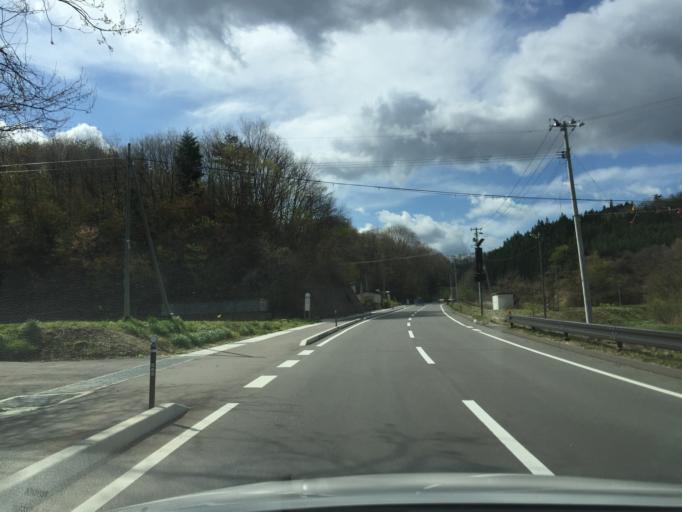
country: JP
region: Fukushima
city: Funehikimachi-funehiki
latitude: 37.6232
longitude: 140.6451
